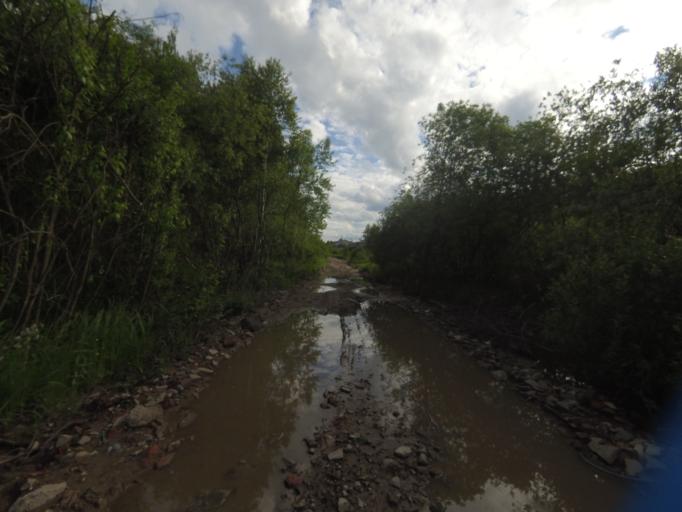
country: RU
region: Moskovskaya
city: Nekrasovskiy
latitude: 56.1024
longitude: 37.5112
